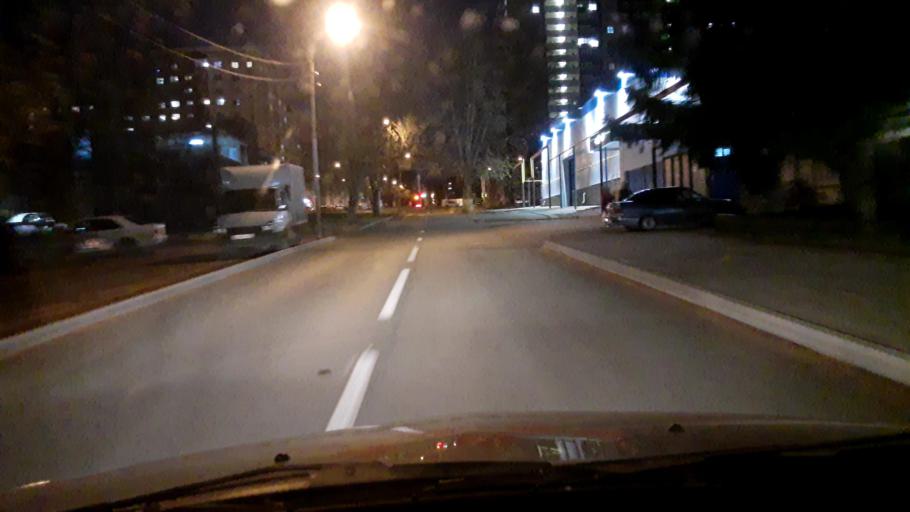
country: RU
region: Bashkortostan
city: Ufa
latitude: 54.8267
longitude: 56.0706
